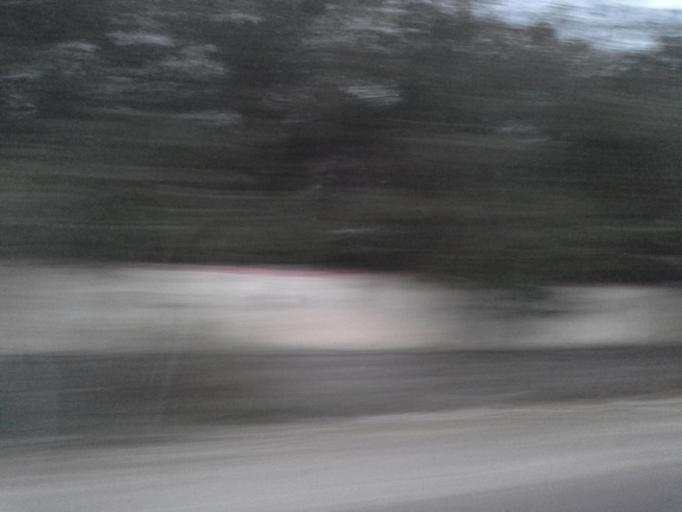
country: IN
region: Telangana
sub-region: Hyderabad
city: Hyderabad
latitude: 17.3229
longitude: 78.3808
